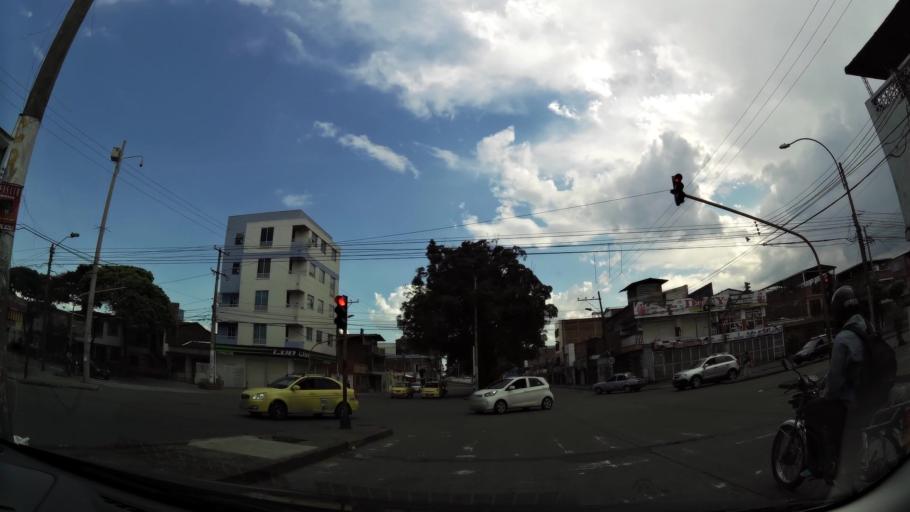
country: CO
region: Valle del Cauca
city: Cali
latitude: 3.4362
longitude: -76.5261
